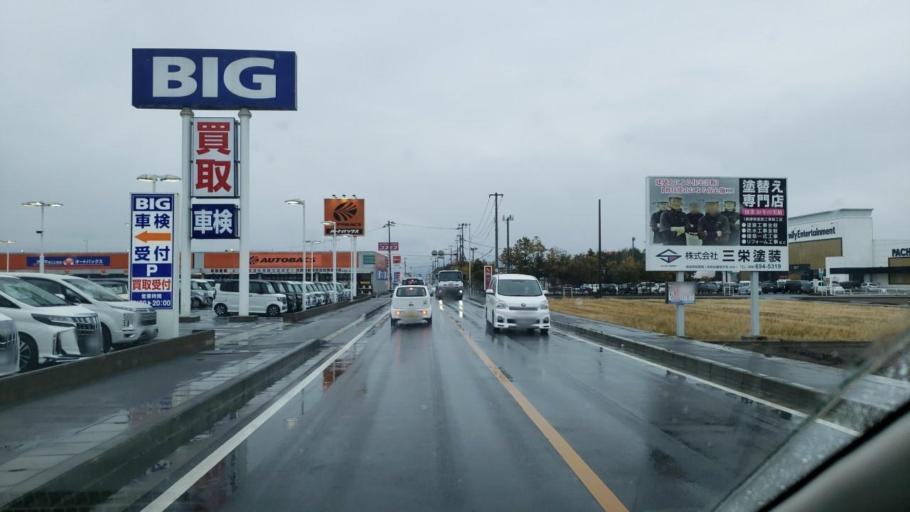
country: JP
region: Tokushima
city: Ishii
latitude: 34.1126
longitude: 134.4363
